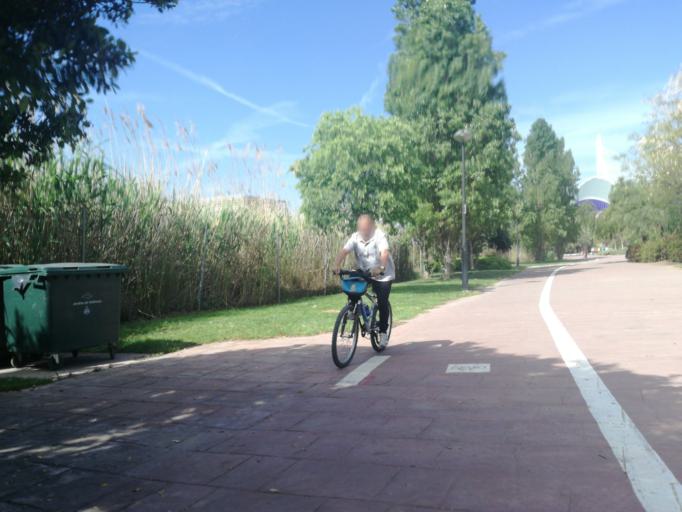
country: ES
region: Valencia
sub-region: Provincia de Valencia
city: Valencia
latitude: 39.4543
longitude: -0.3425
